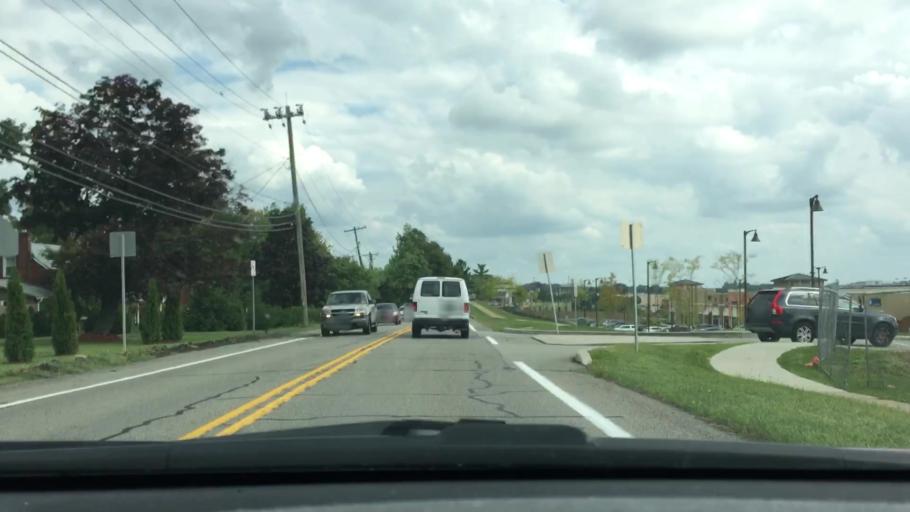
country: US
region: Pennsylvania
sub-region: Allegheny County
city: Mount Lebanon
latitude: 40.3488
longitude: -80.0580
